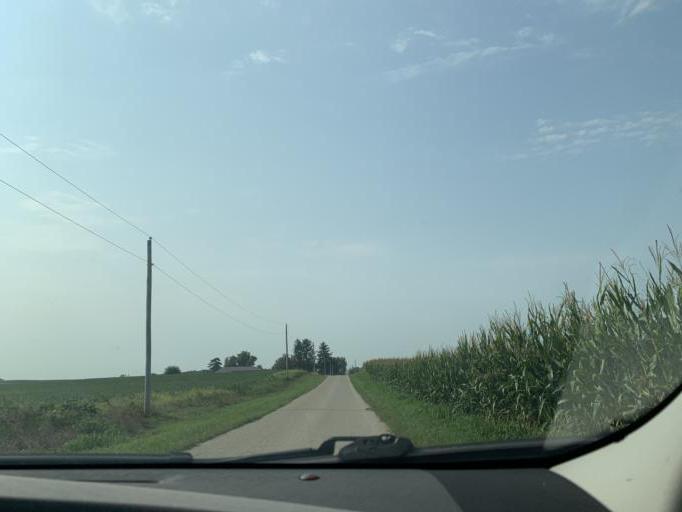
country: US
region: Illinois
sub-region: Whiteside County
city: Morrison
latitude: 41.8582
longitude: -89.8718
